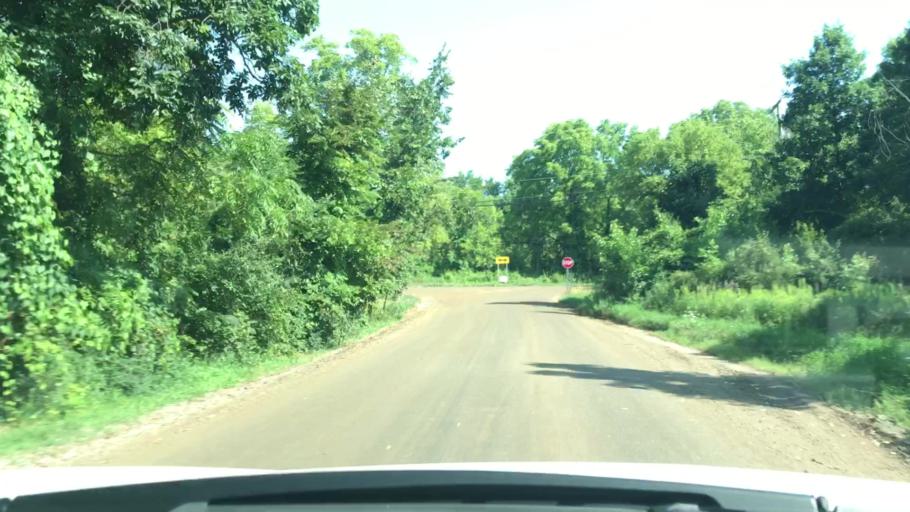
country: US
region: Michigan
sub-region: Oakland County
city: Oxford
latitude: 42.7850
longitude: -83.3424
